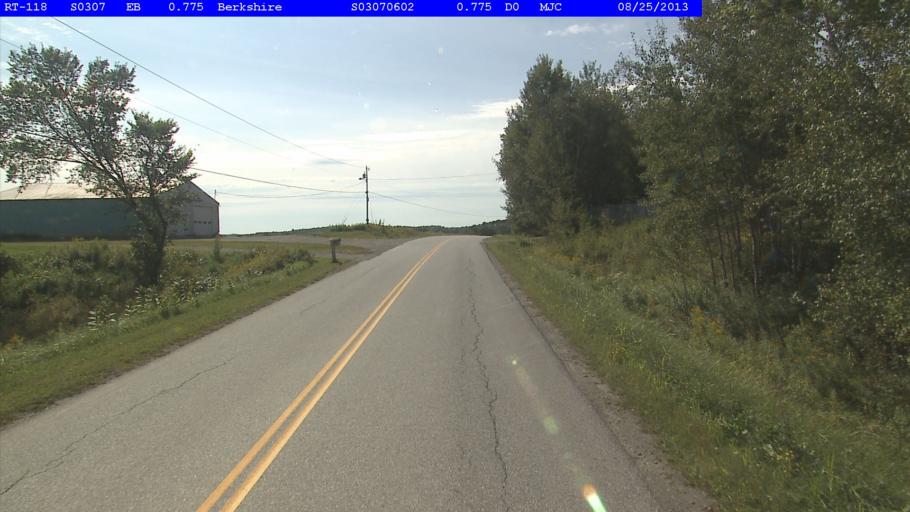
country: US
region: Vermont
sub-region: Franklin County
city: Richford
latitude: 44.9356
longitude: -72.7269
